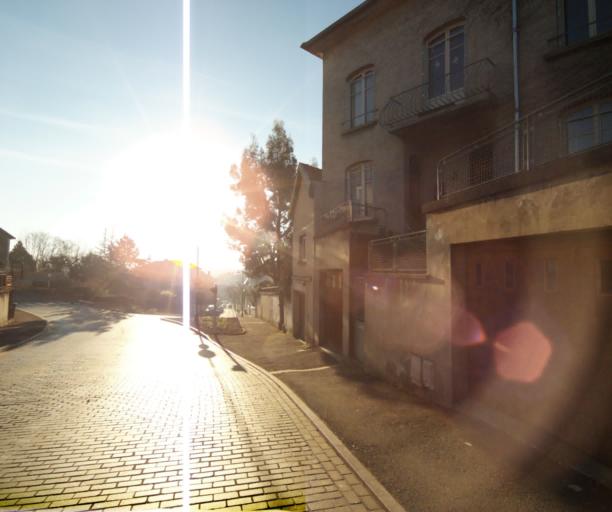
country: FR
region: Lorraine
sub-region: Departement de Meurthe-et-Moselle
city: Laxou
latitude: 48.6850
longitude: 6.1465
